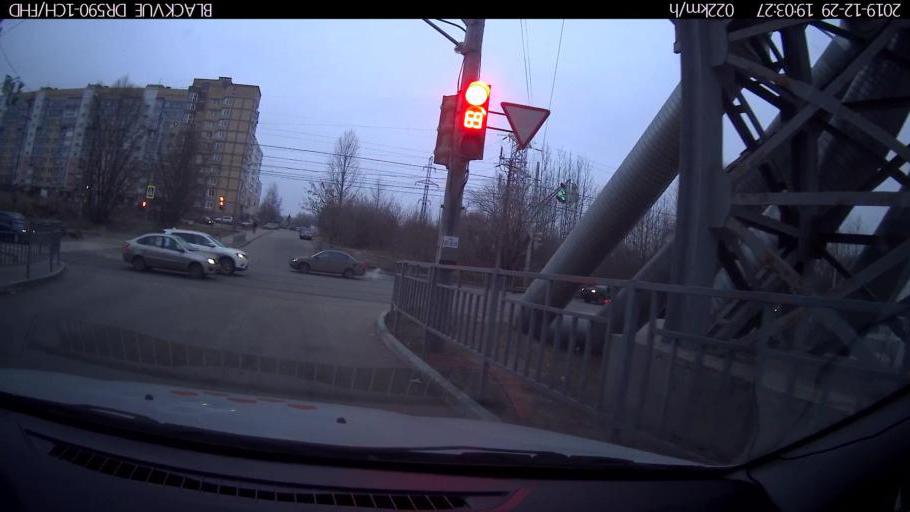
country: RU
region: Nizjnij Novgorod
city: Nizhniy Novgorod
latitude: 56.3406
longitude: 43.9127
